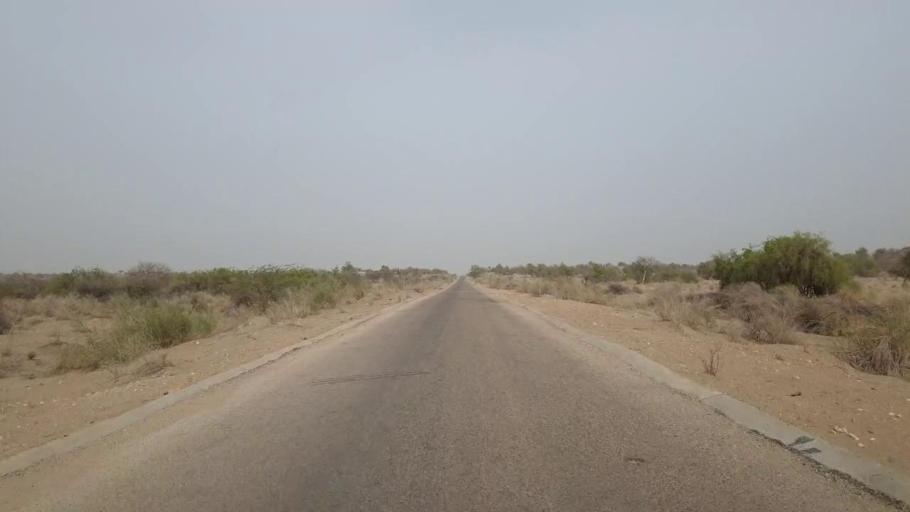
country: PK
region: Sindh
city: Islamkot
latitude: 24.5616
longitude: 70.3388
